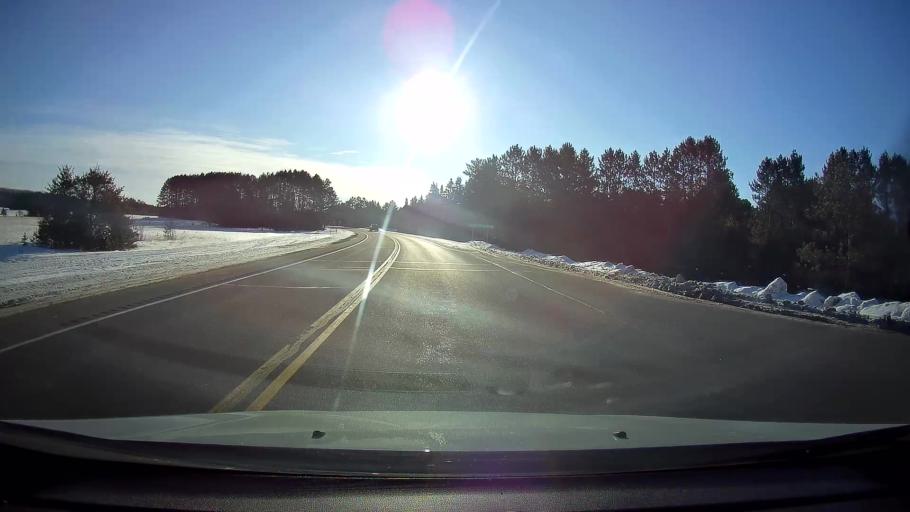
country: US
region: Wisconsin
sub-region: Sawyer County
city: Hayward
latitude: 45.9881
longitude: -91.5911
